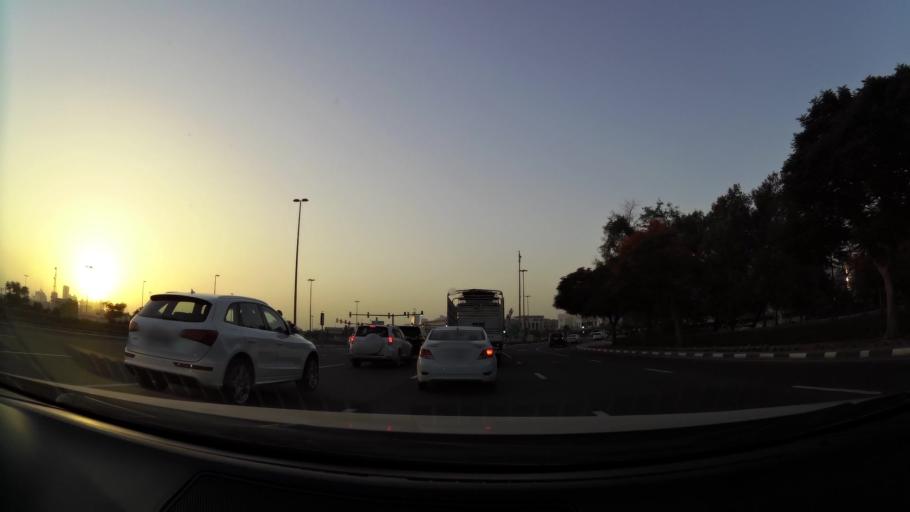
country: AE
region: Ash Shariqah
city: Sharjah
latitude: 25.2449
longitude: 55.3223
